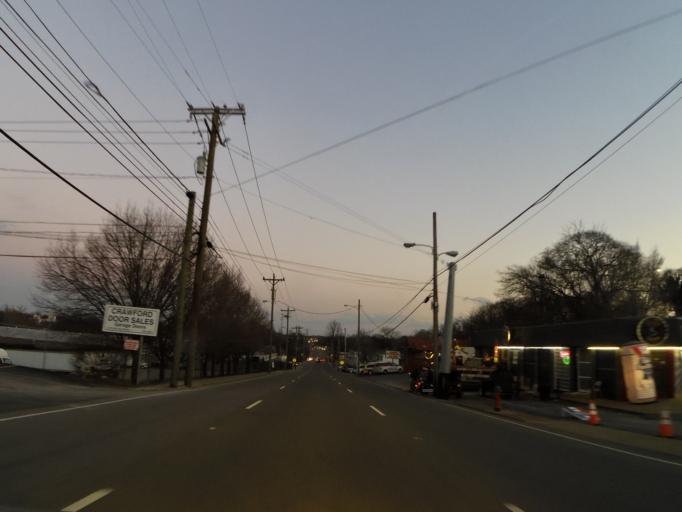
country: US
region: Tennessee
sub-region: Davidson County
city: Nashville
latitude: 36.1402
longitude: -86.7635
